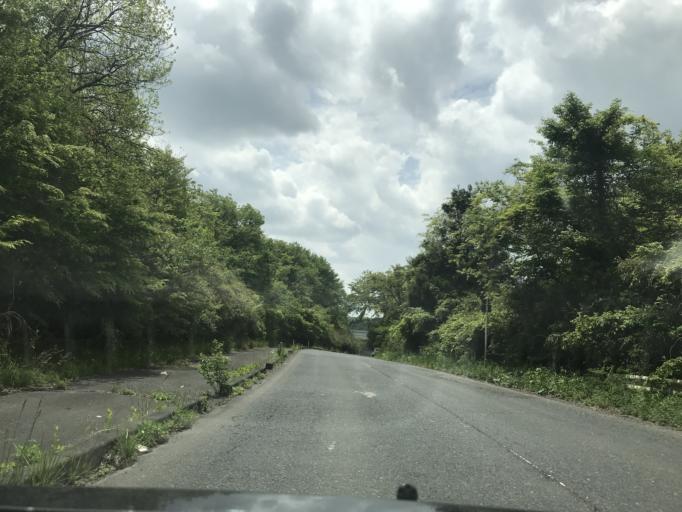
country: JP
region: Miyagi
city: Furukawa
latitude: 38.7007
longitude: 140.9267
